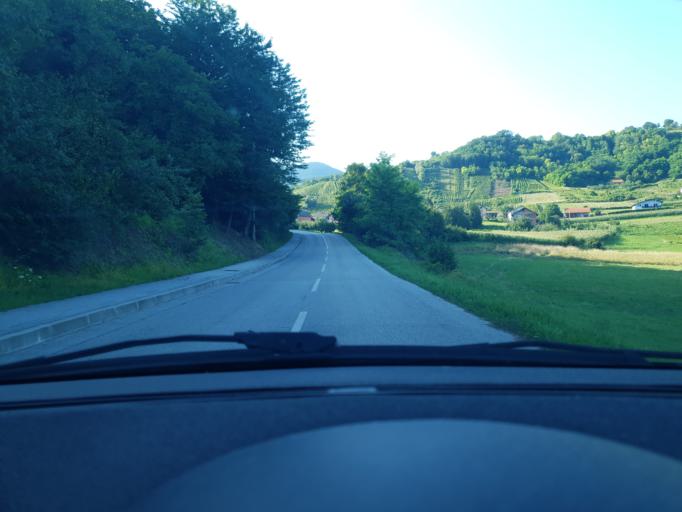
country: HR
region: Krapinsko-Zagorska
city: Radoboj
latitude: 46.1605
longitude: 15.9371
